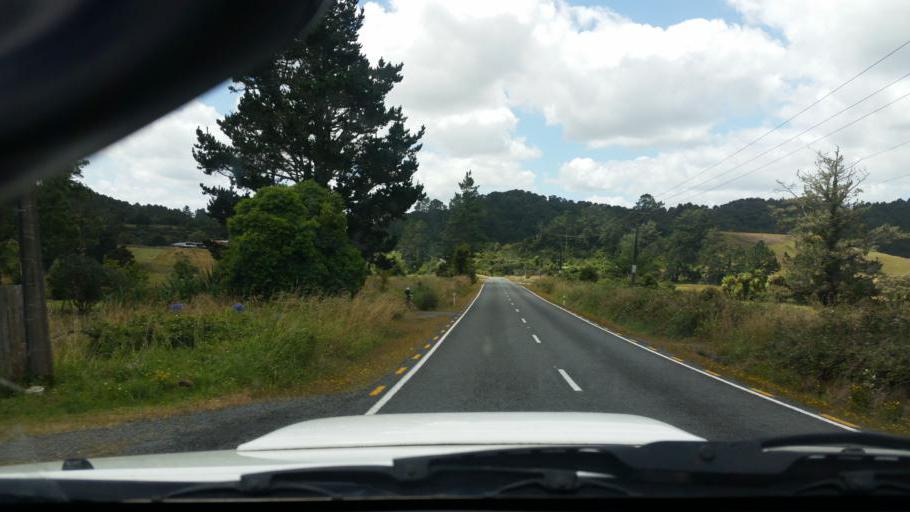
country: NZ
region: Northland
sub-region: Whangarei
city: Ruakaka
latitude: -36.0418
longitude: 174.2791
